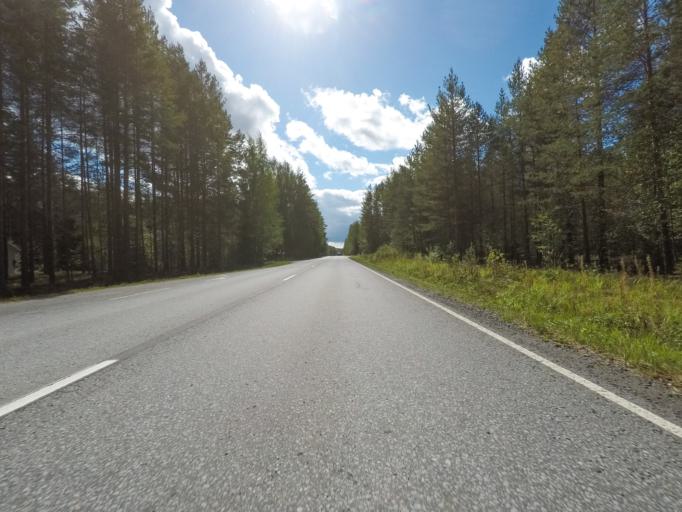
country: FI
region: Central Finland
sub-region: Jyvaeskylae
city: Toivakka
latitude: 62.1208
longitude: 26.0990
